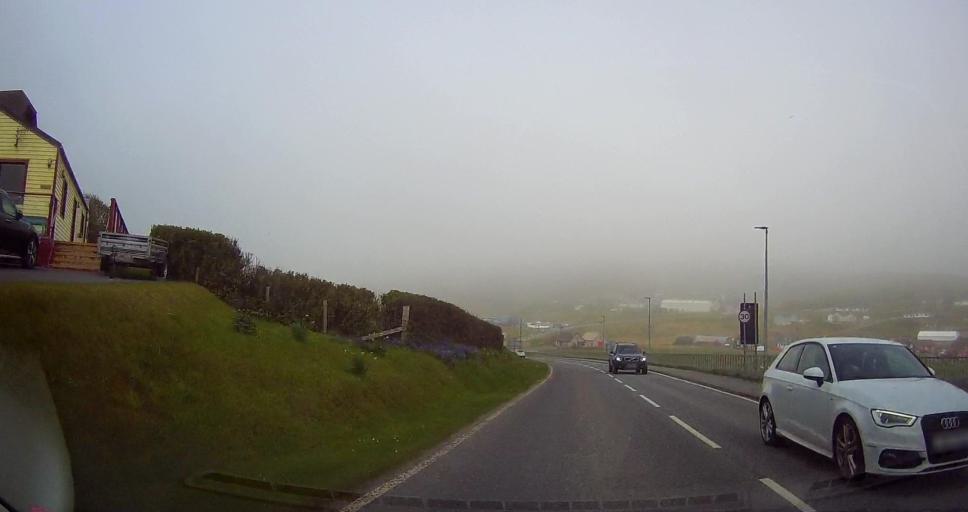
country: GB
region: Scotland
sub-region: Shetland Islands
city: Lerwick
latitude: 60.1406
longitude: -1.2708
